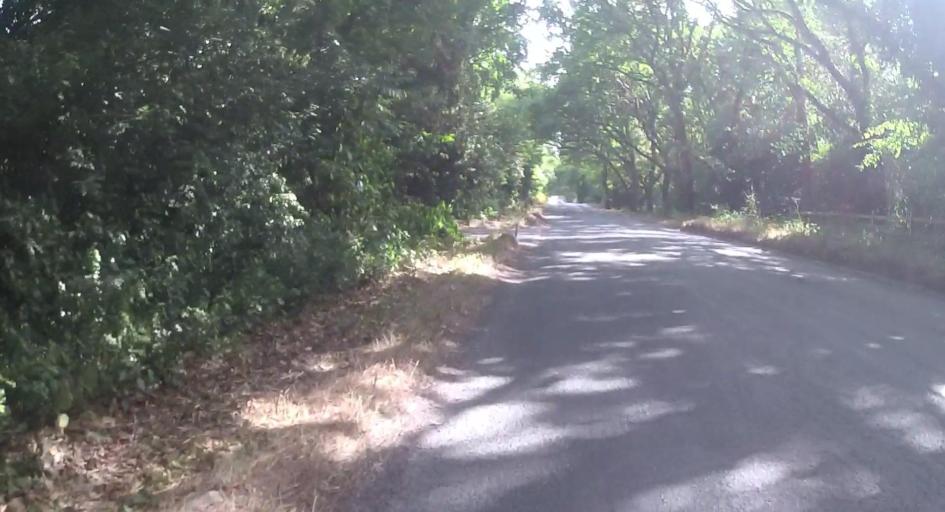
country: GB
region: England
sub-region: Dorset
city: Wareham
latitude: 50.6643
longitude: -2.1150
